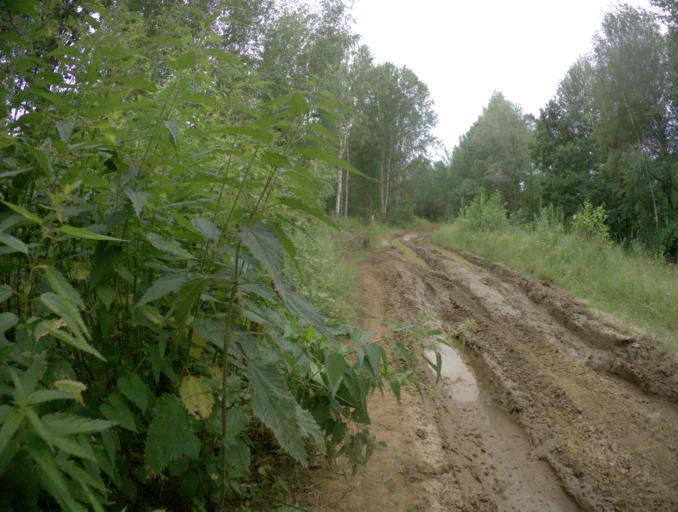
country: RU
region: Vladimir
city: Gorokhovets
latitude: 56.2161
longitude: 42.6722
